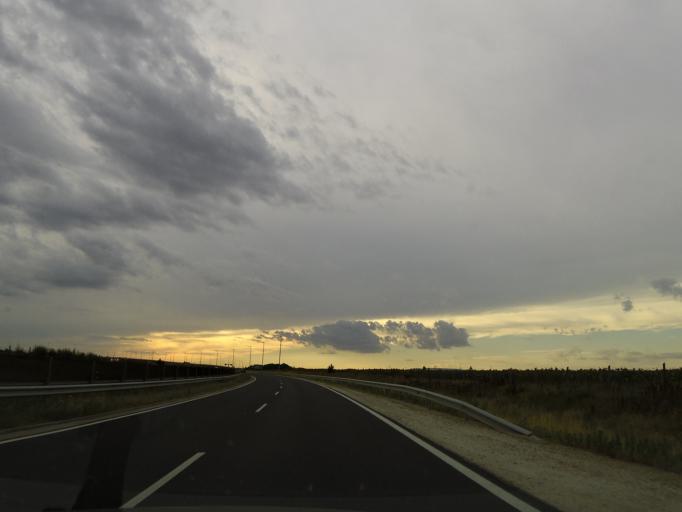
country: HU
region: Pest
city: Vecses
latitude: 47.4210
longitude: 19.2732
